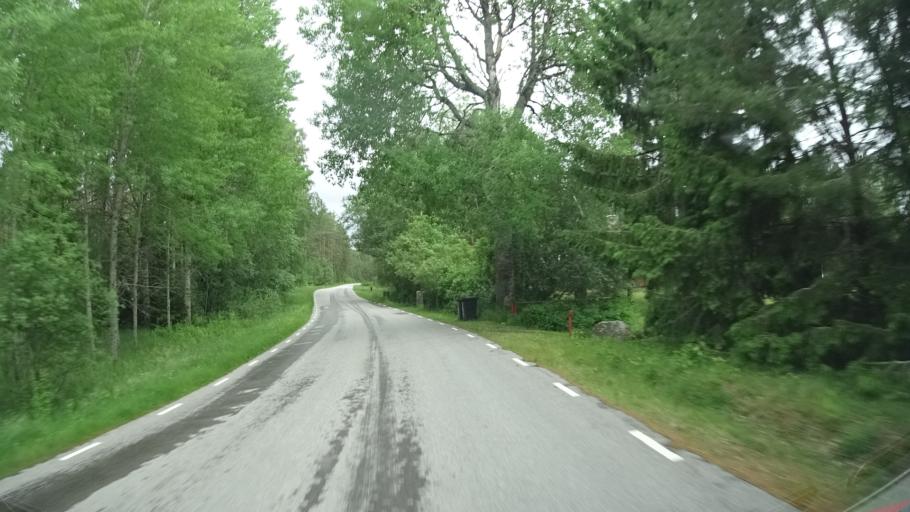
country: SE
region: Joenkoeping
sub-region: Eksjo Kommun
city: Mariannelund
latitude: 57.6993
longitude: 15.6566
